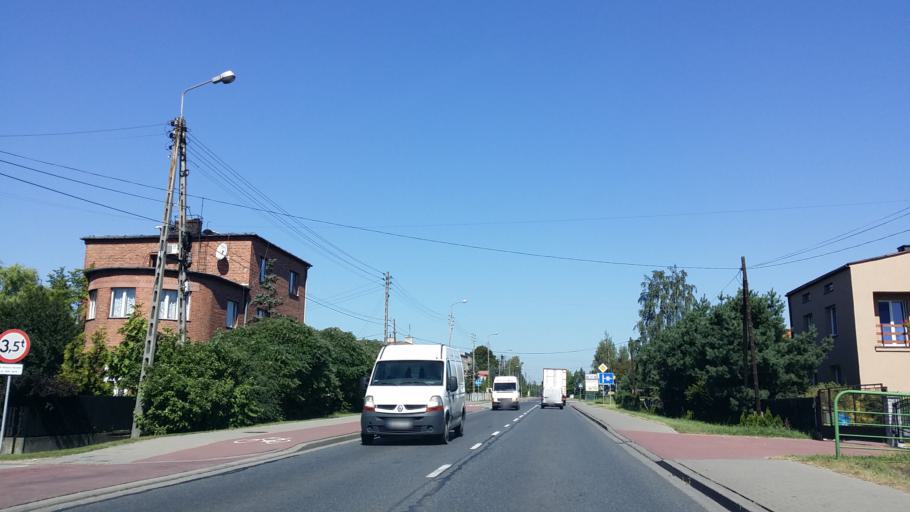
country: PL
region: Silesian Voivodeship
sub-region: Powiat bierunsko-ledzinski
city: Imielin
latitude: 50.1517
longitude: 19.1815
